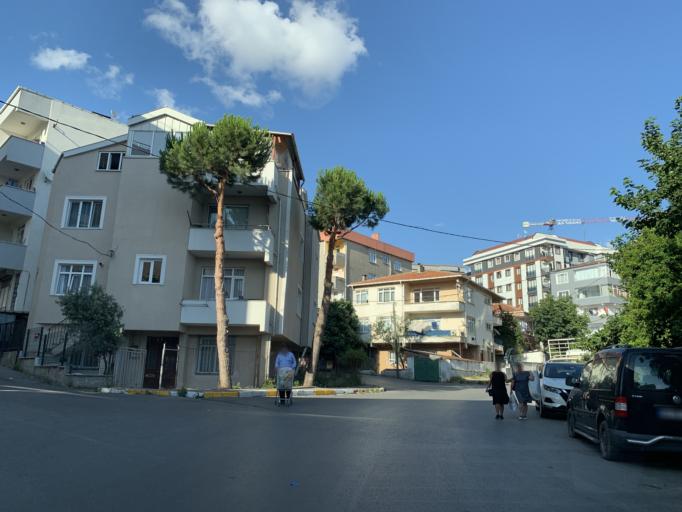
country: TR
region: Istanbul
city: Pendik
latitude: 40.8933
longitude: 29.2488
